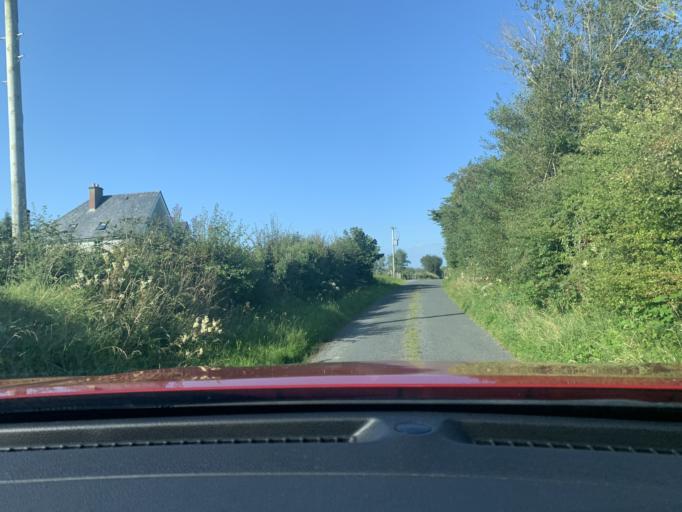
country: IE
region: Connaught
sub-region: Sligo
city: Tobercurry
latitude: 54.0639
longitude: -8.7821
